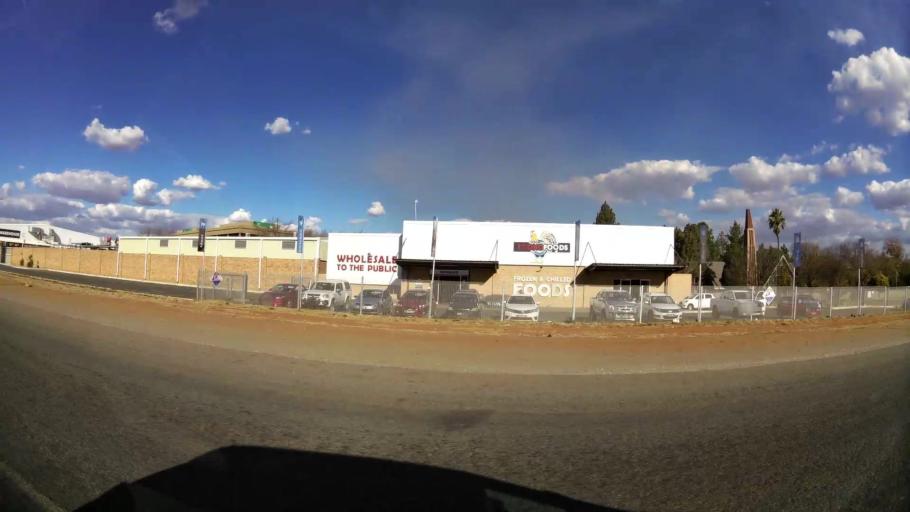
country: ZA
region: North-West
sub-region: Dr Kenneth Kaunda District Municipality
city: Klerksdorp
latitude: -26.8573
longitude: 26.6748
